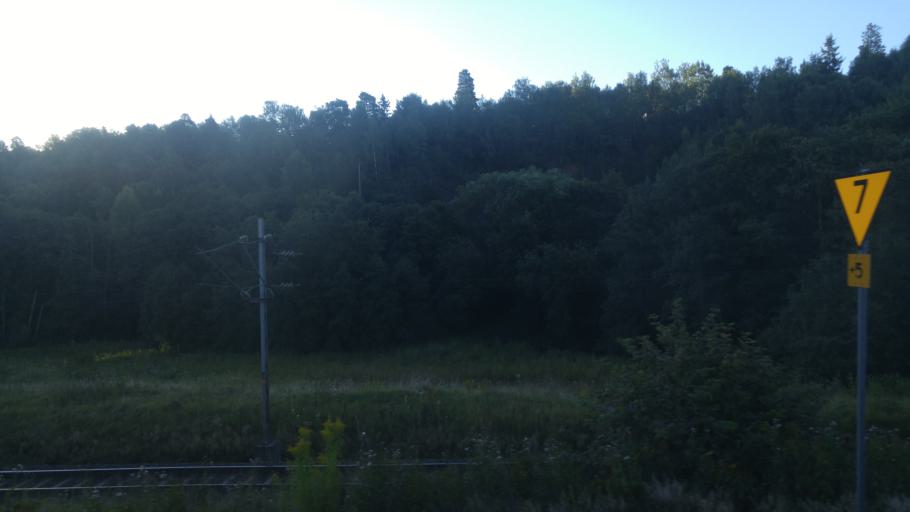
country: NO
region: Oslo
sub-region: Oslo
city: Oslo
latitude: 59.9136
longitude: 10.8276
